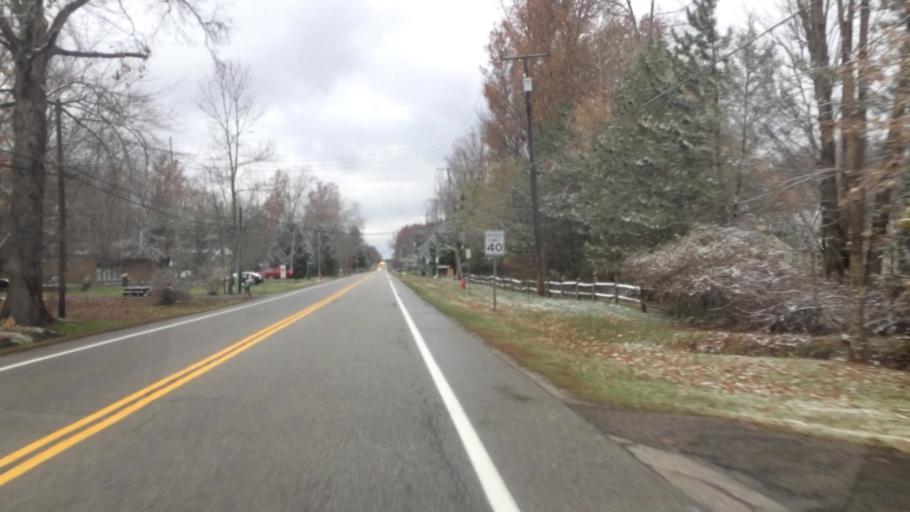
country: US
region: Ohio
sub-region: Summit County
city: Macedonia
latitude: 41.2992
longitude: -81.5268
